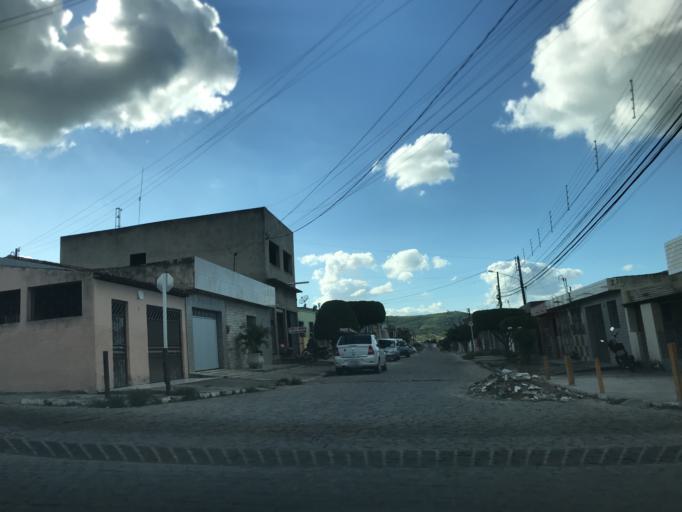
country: BR
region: Pernambuco
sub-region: Bezerros
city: Bezerros
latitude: -8.2450
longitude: -35.7578
